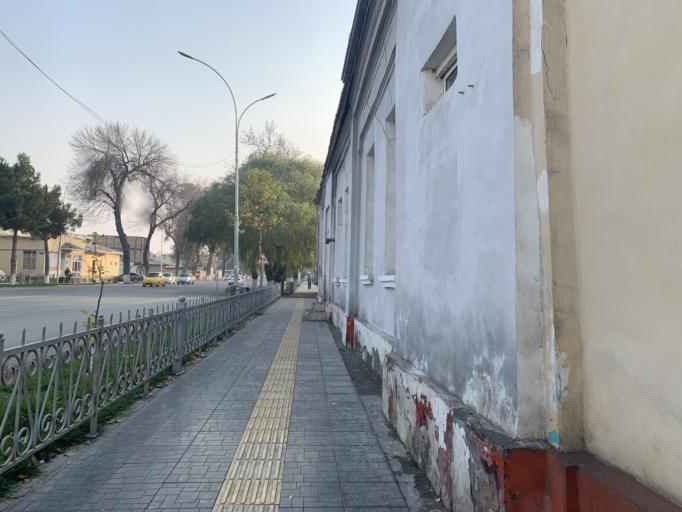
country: UZ
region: Fergana
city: Qo`qon
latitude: 40.5335
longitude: 70.9376
